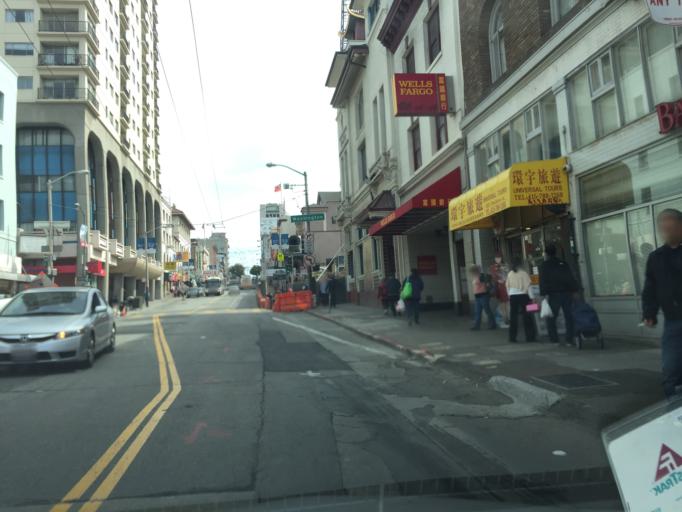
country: US
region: California
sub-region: San Francisco County
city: San Francisco
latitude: 37.7958
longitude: -122.4086
